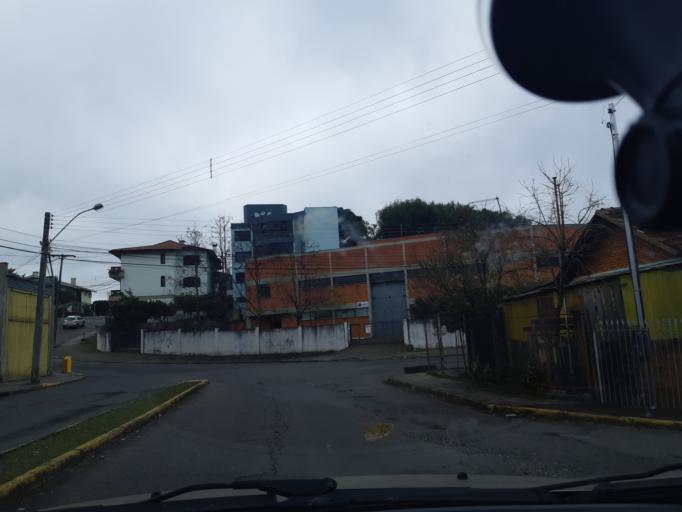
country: BR
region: Rio Grande do Sul
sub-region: Caxias Do Sul
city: Caxias do Sul
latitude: -29.1543
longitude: -51.2069
